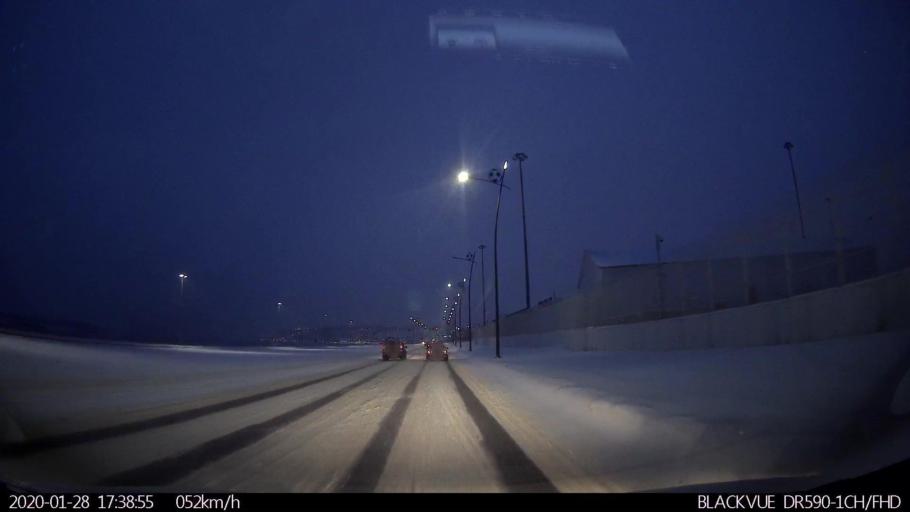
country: RU
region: Nizjnij Novgorod
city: Nizhniy Novgorod
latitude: 56.3385
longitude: 43.9665
